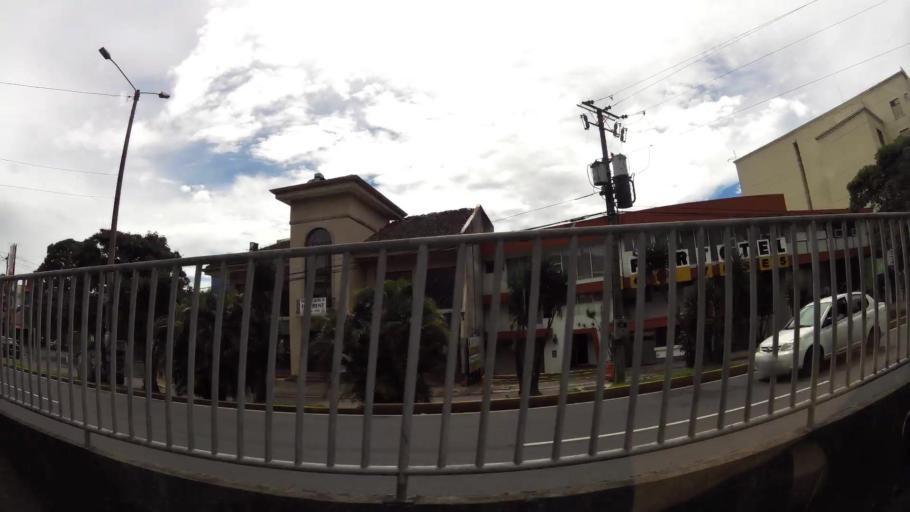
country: CR
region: San Jose
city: San Pedro
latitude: 9.9325
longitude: -84.0574
